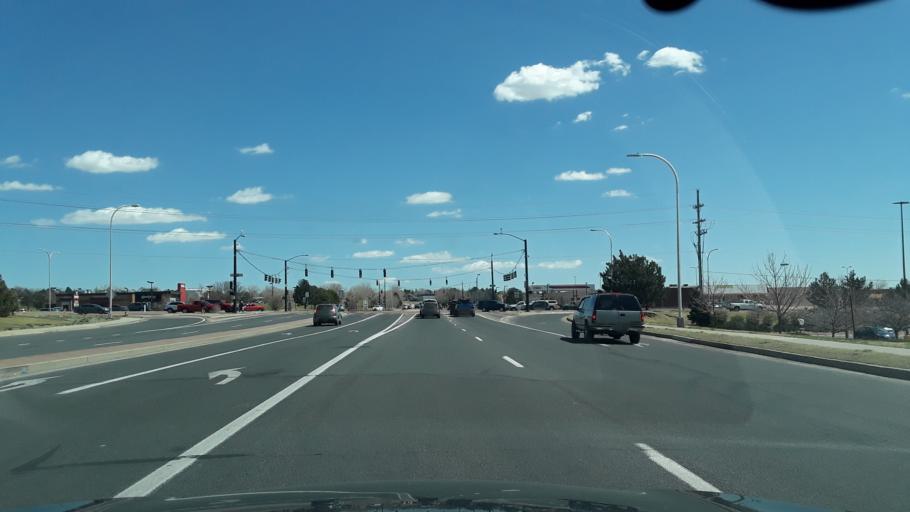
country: US
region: Colorado
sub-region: El Paso County
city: Cimarron Hills
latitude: 38.8571
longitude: -104.7216
